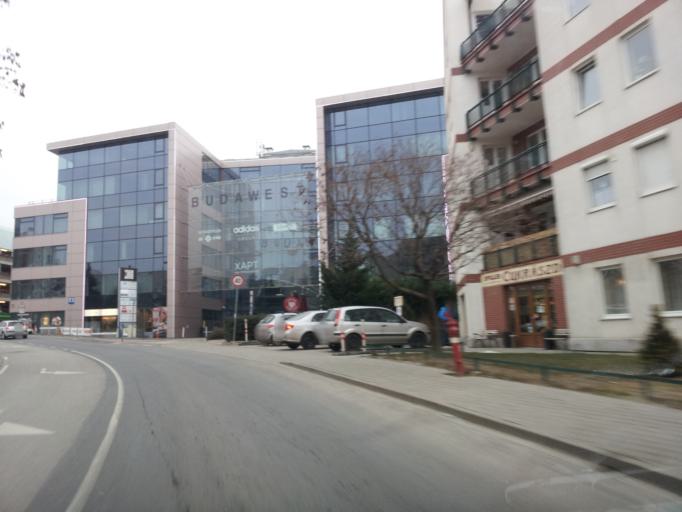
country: HU
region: Budapest
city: Budapest XII. keruelet
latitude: 47.4652
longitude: 19.0061
